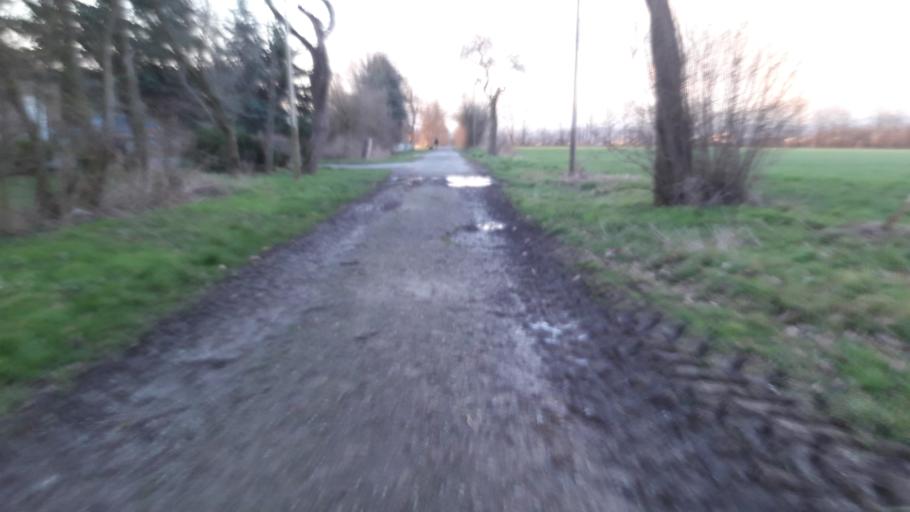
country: DE
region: North Rhine-Westphalia
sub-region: Regierungsbezirk Detmold
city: Paderborn
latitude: 51.6923
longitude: 8.7743
